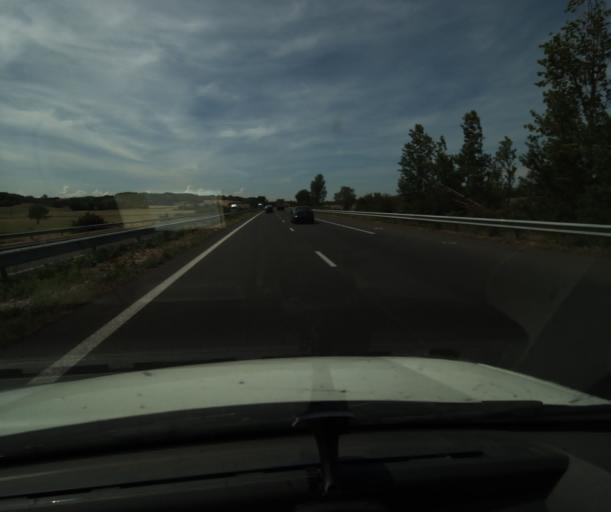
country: FR
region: Midi-Pyrenees
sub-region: Departement de la Haute-Garonne
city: Avignonet-Lauragais
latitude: 43.3256
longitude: 1.8554
